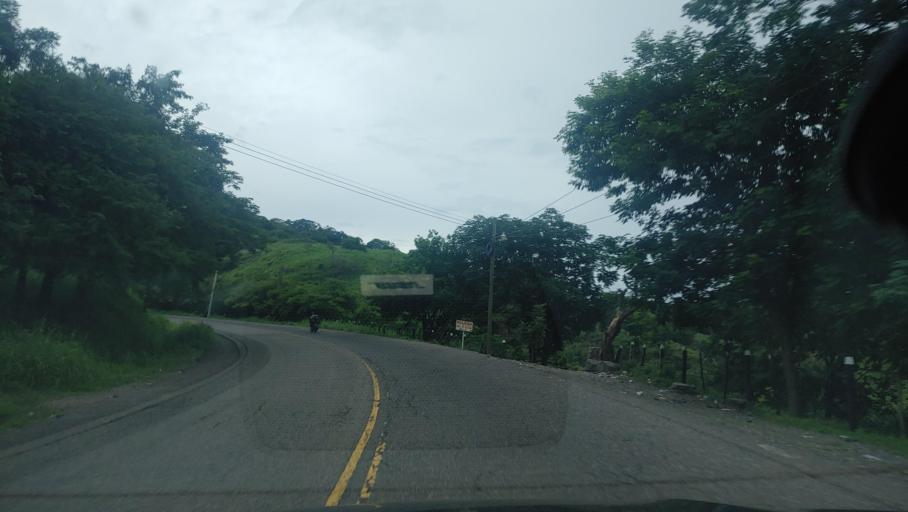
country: HN
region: Choluteca
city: Corpus
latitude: 13.3702
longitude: -87.0591
